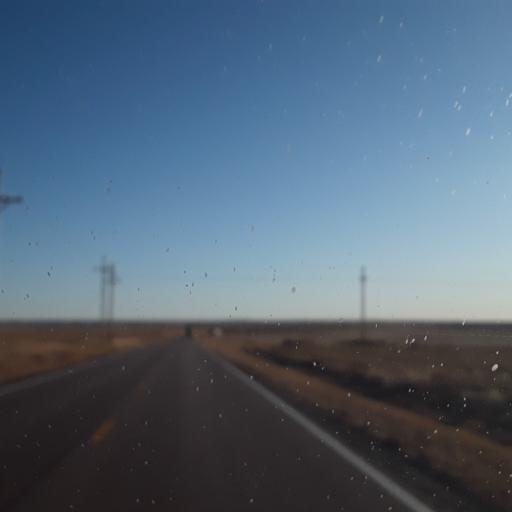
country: US
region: Kansas
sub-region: Wallace County
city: Sharon Springs
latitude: 38.9684
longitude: -101.7396
